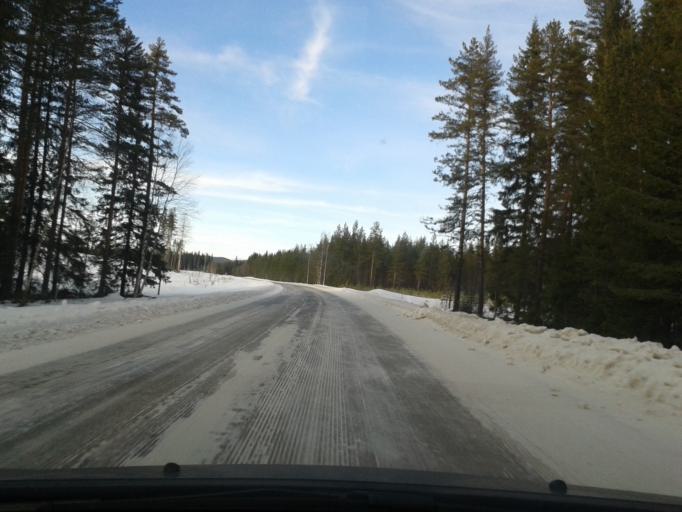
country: SE
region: Vaesternorrland
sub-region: OErnskoeldsviks Kommun
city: Bredbyn
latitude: 63.5940
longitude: 17.9189
